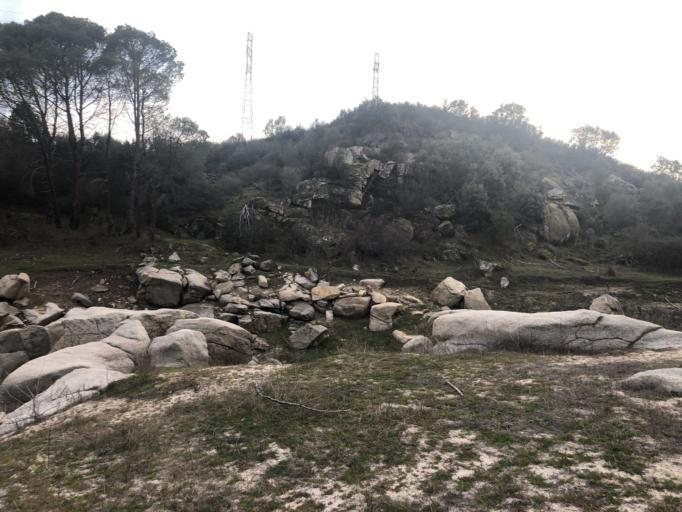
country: ES
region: Madrid
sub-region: Provincia de Madrid
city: San Martin de Valdeiglesias
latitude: 40.4018
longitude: -4.4235
